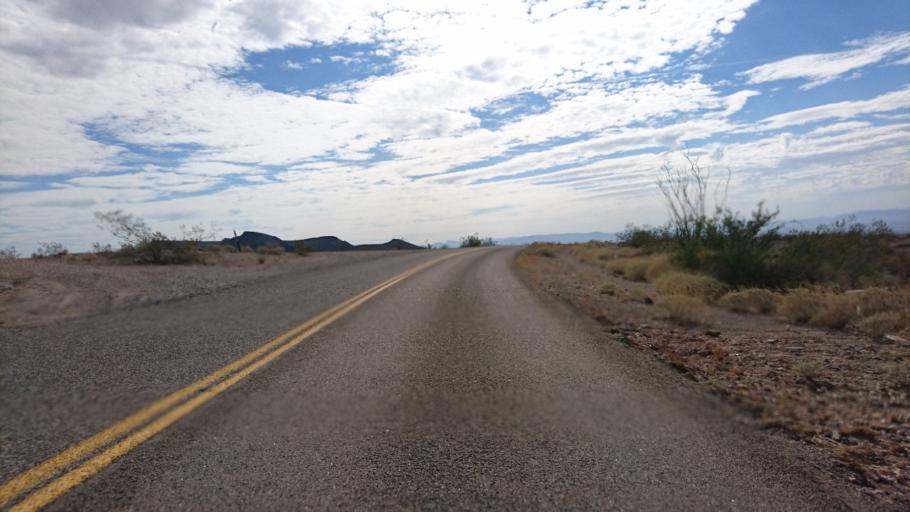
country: US
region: Arizona
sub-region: Mohave County
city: Mohave Valley
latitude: 34.9541
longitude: -114.4100
